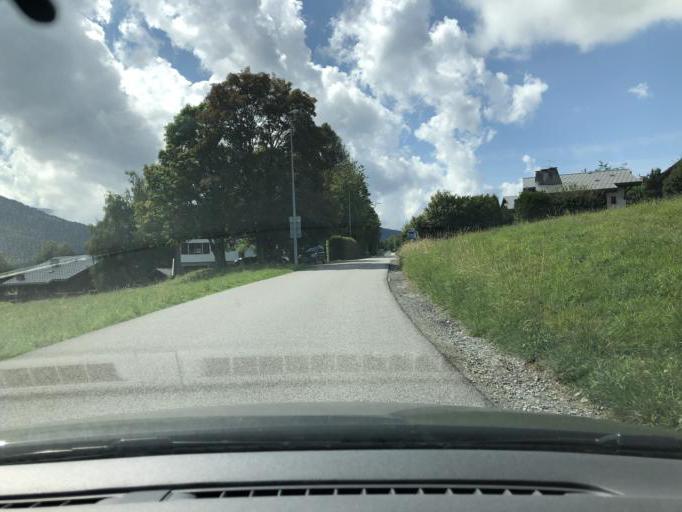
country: FR
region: Rhone-Alpes
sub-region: Departement de la Haute-Savoie
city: Combloux
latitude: 45.8891
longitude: 6.6367
